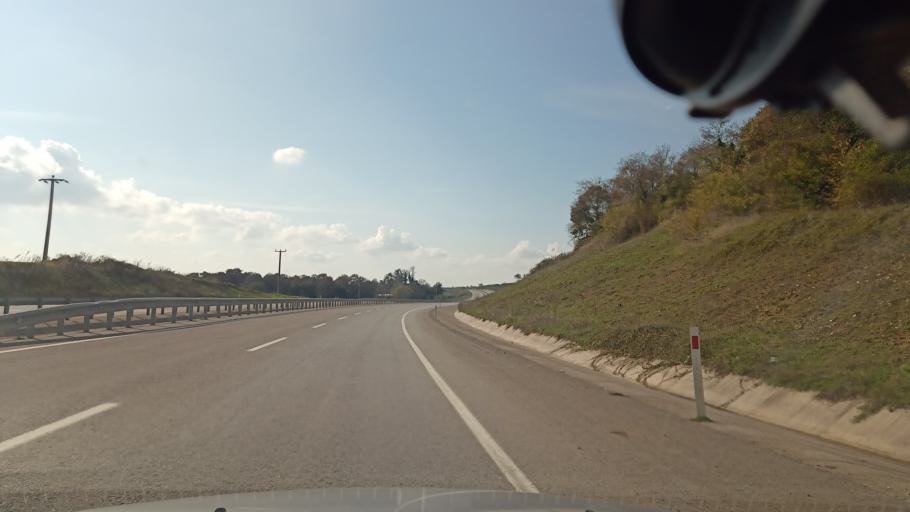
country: TR
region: Sakarya
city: Kaynarca
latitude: 41.0601
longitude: 30.3514
